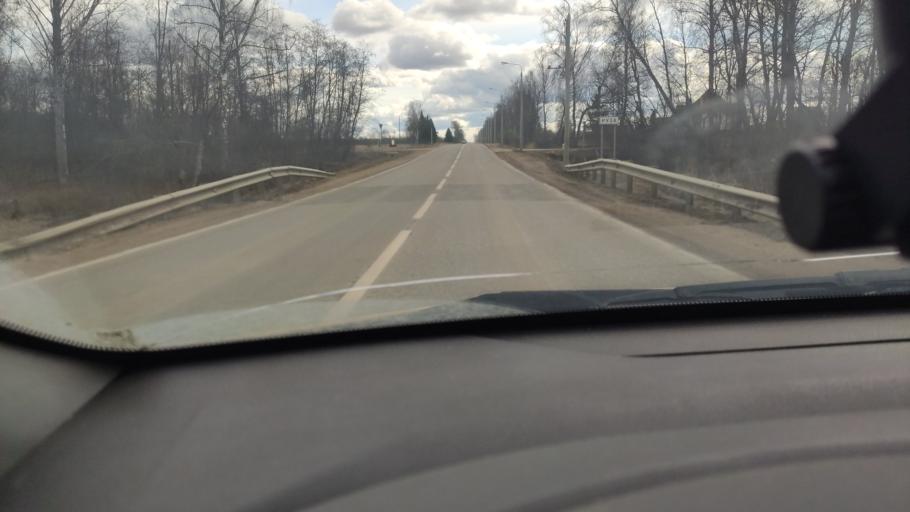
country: RU
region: Moskovskaya
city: Ruza
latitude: 55.7179
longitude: 36.1675
